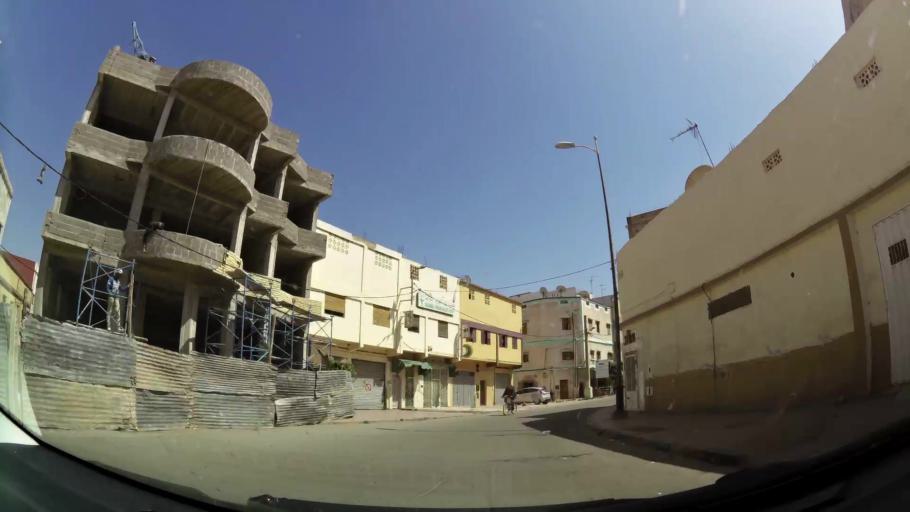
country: MA
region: Souss-Massa-Draa
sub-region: Inezgane-Ait Mellou
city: Inezgane
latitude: 30.3512
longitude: -9.5353
